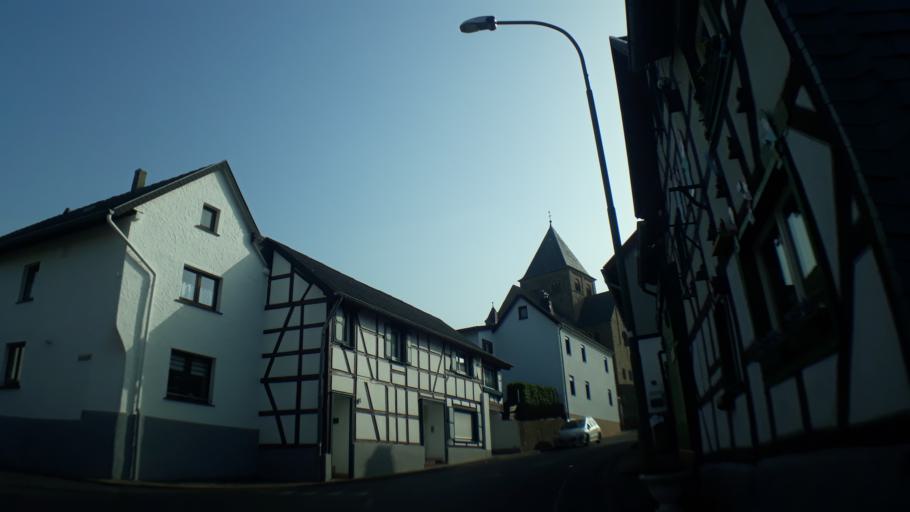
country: DE
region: North Rhine-Westphalia
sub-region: Regierungsbezirk Koln
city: Bad Munstereifel
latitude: 50.5492
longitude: 6.7228
